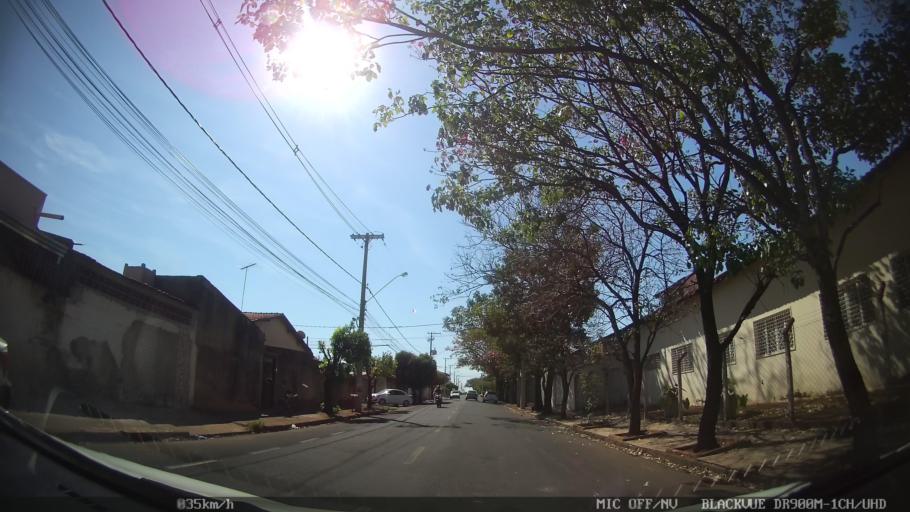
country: BR
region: Sao Paulo
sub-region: Sao Jose Do Rio Preto
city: Sao Jose do Rio Preto
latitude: -20.7800
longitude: -49.4199
